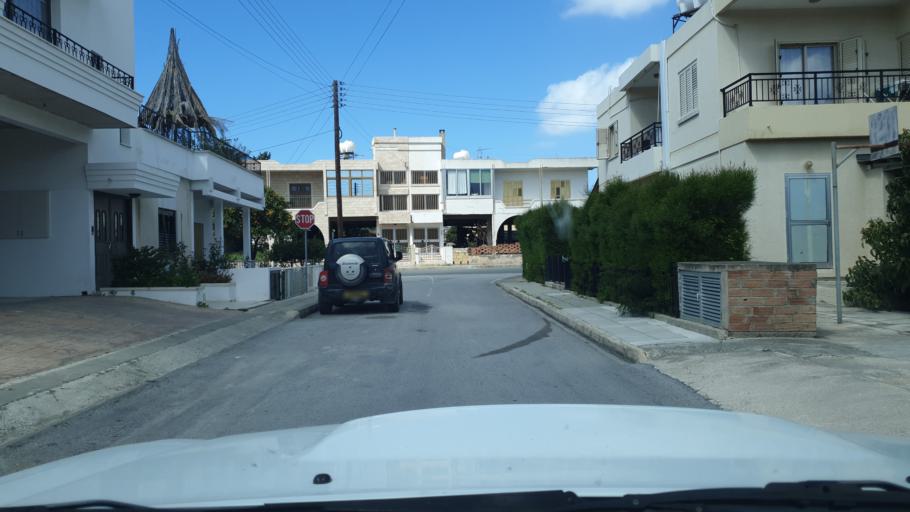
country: CY
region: Pafos
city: Paphos
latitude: 34.7622
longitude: 32.4480
